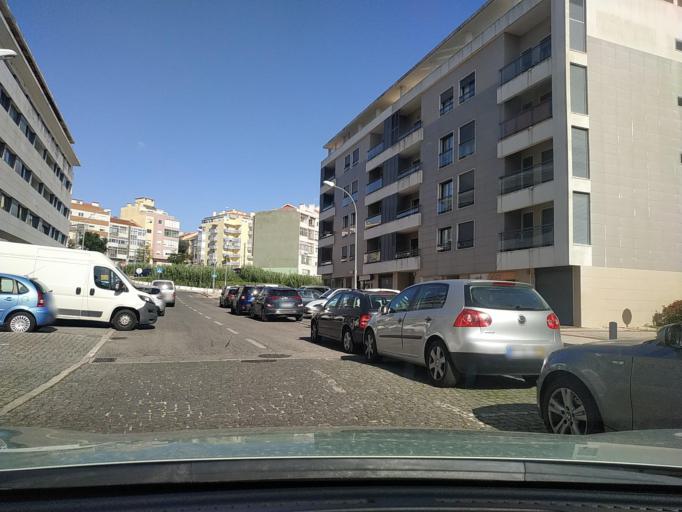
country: PT
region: Lisbon
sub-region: Sintra
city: Queluz
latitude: 38.7610
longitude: -9.2425
